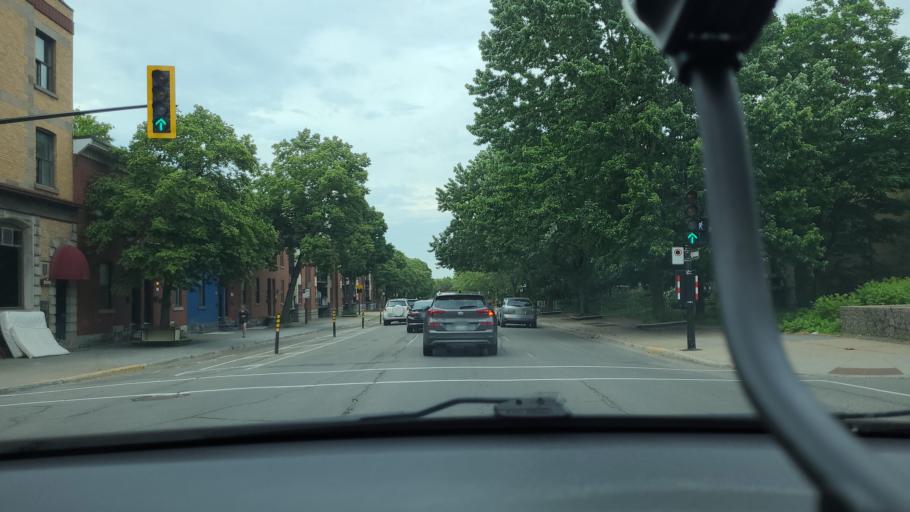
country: CA
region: Quebec
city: Westmount
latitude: 45.4853
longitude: -73.5770
